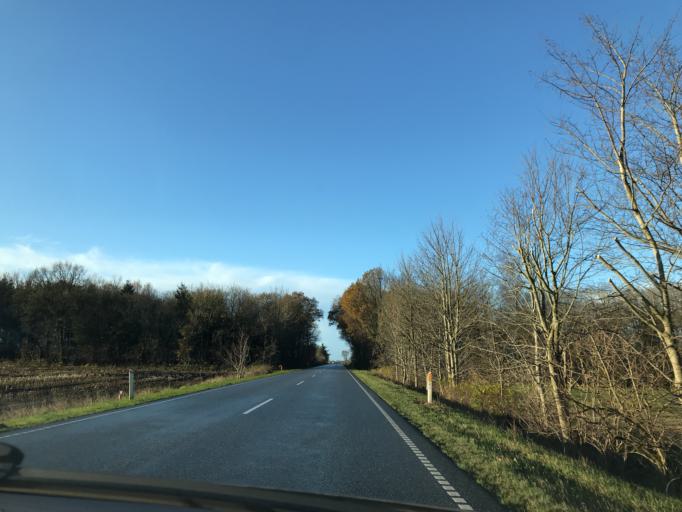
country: DK
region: South Denmark
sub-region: Tonder Kommune
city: Toftlund
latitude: 55.1342
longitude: 9.1582
